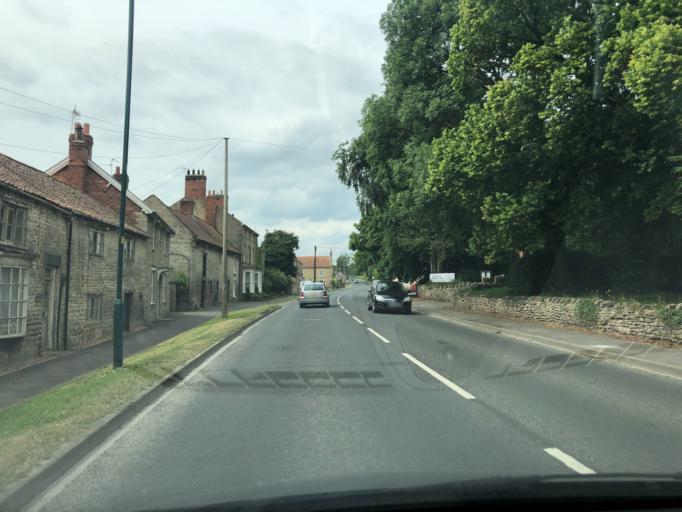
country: GB
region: England
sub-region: North Yorkshire
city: Pickering
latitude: 54.2577
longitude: -0.8010
